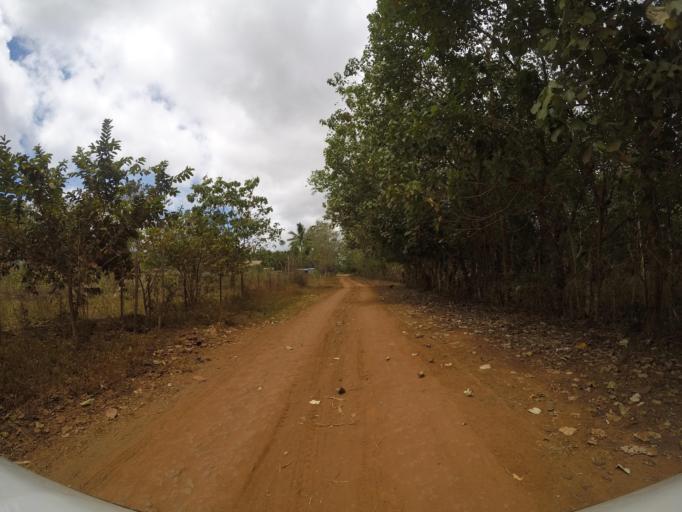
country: TL
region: Lautem
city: Lospalos
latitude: -8.4740
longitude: 126.9914
